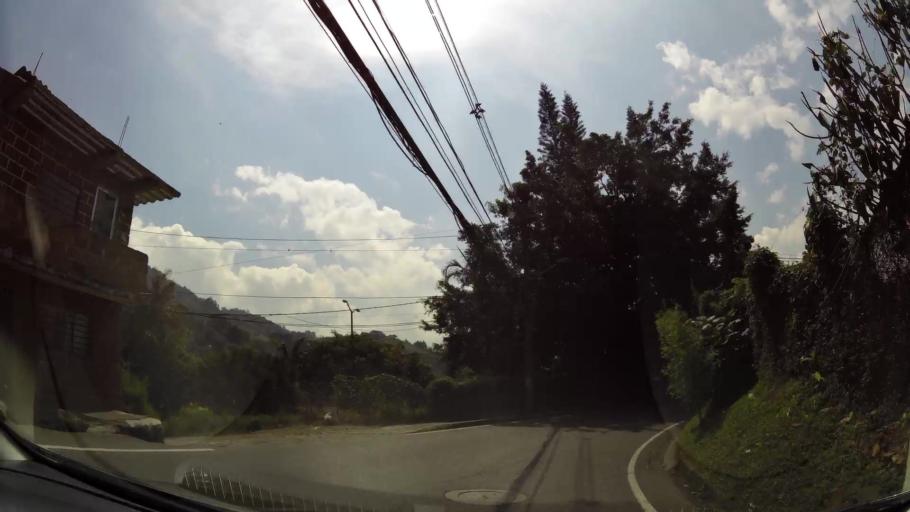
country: CO
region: Antioquia
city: La Estrella
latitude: 6.1816
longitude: -75.6399
